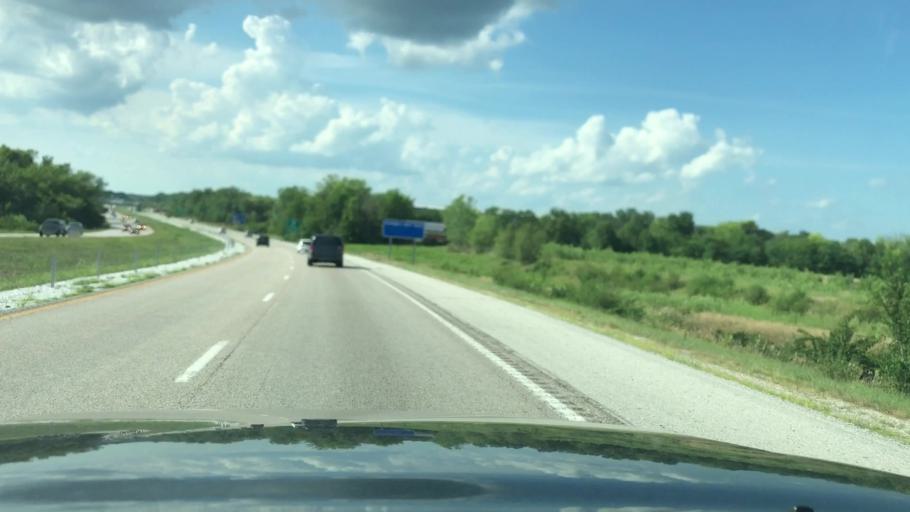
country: US
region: Missouri
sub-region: Saint Charles County
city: Wentzville
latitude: 38.8161
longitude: -90.8431
